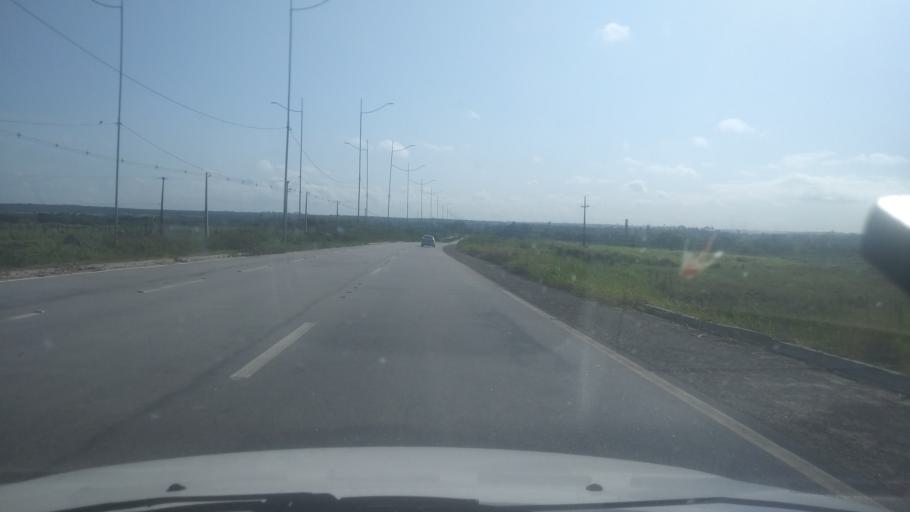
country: BR
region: Rio Grande do Norte
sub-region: Macaiba
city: Macaiba
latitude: -5.8202
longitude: -35.3660
